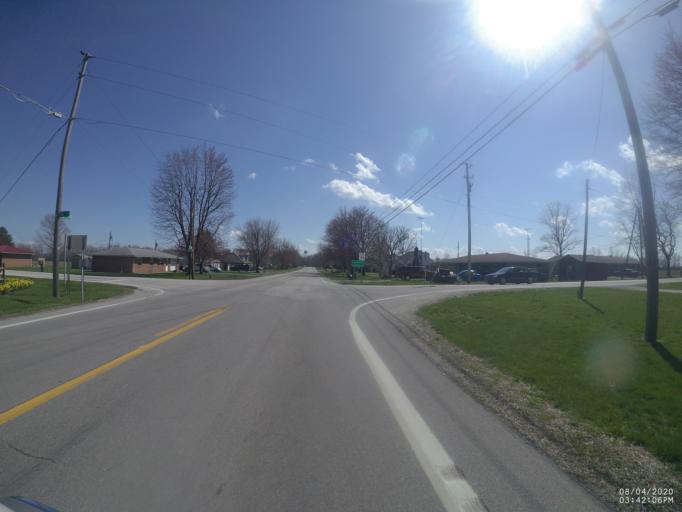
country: US
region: Ohio
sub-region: Sandusky County
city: Stony Prairie
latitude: 41.2532
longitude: -83.2356
